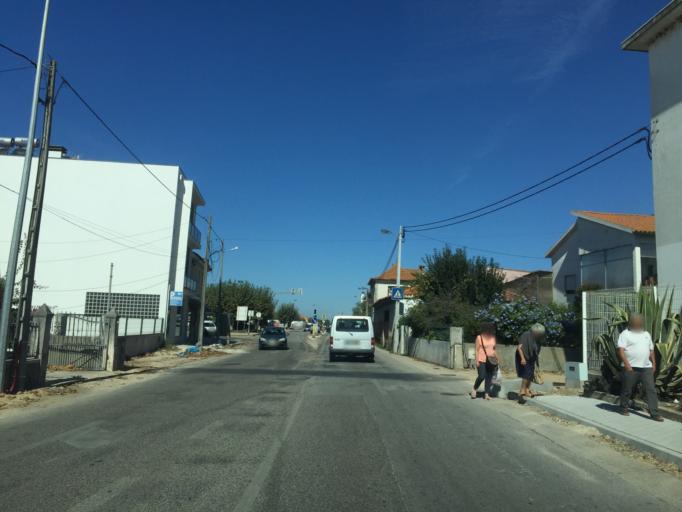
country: PT
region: Coimbra
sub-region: Montemor-O-Velho
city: Arazede
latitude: 40.3124
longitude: -8.7539
